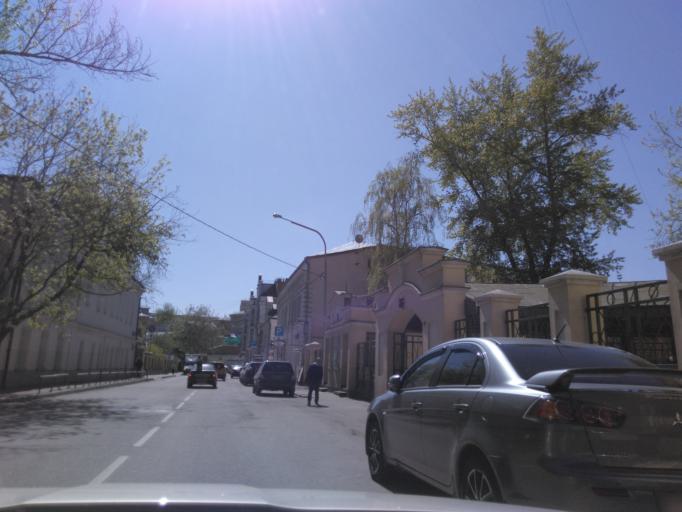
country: RU
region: Moscow
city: Zamoskvorech'ye
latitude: 55.7271
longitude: 37.6311
